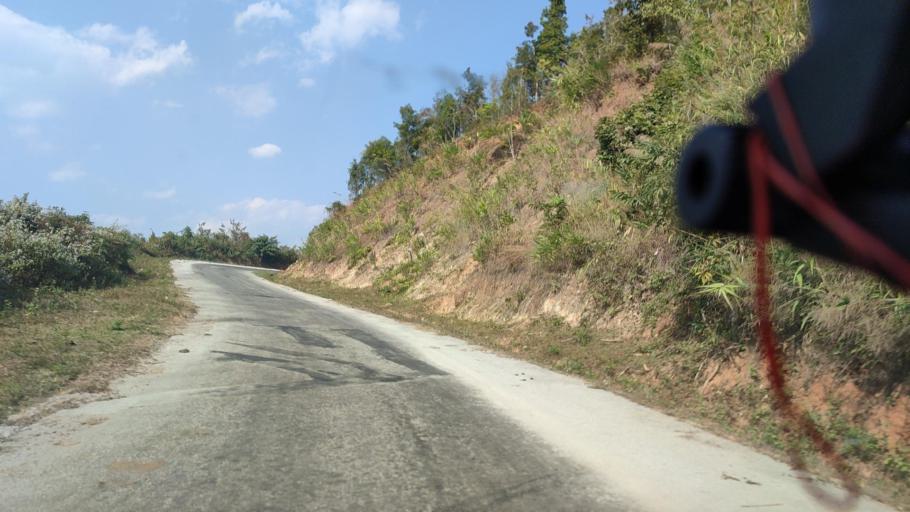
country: CN
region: Yunnan
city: Menghai
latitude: 21.4501
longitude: 99.6561
